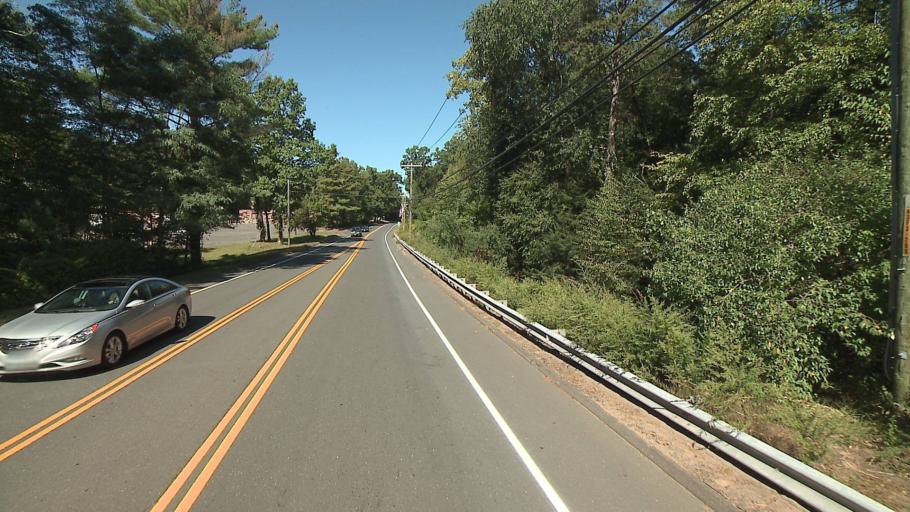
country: US
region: Connecticut
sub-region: Hartford County
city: Tariffville
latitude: 41.9097
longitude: -72.7885
